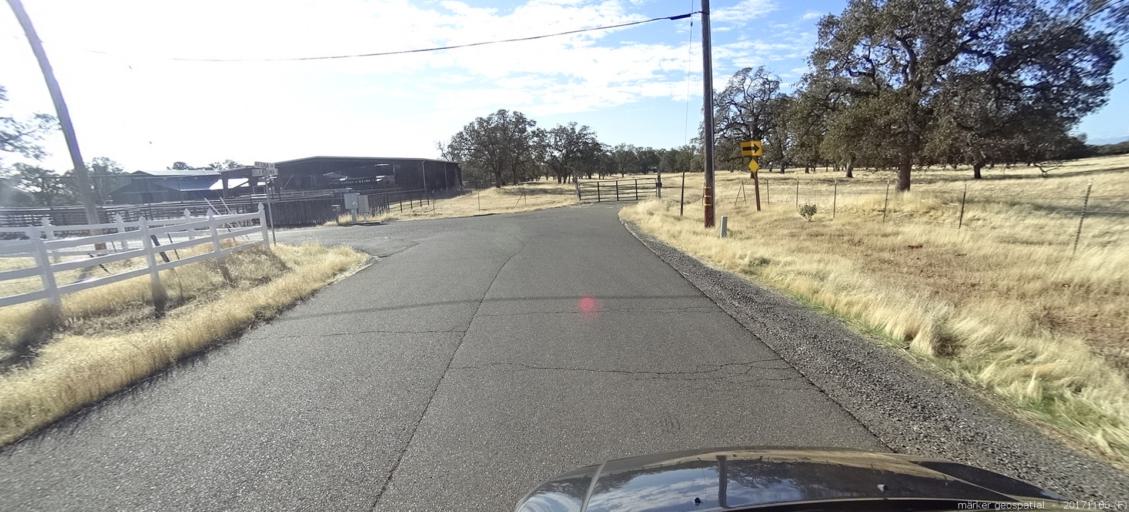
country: US
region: California
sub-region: Shasta County
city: Palo Cedro
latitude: 40.5116
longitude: -122.2482
